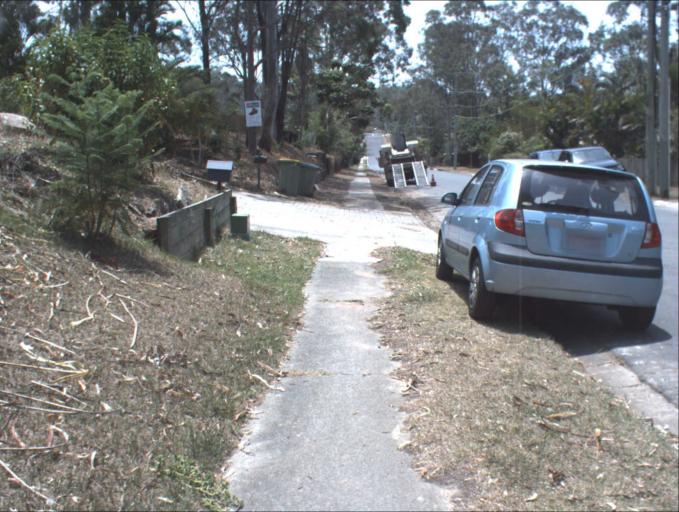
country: AU
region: Queensland
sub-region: Logan
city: Beenleigh
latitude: -27.6632
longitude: 153.1995
